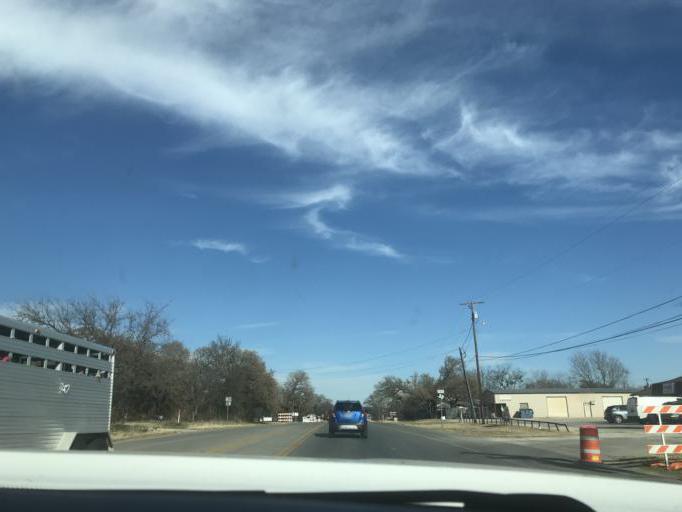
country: US
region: Texas
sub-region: Erath County
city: Stephenville
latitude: 32.2324
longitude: -98.2094
